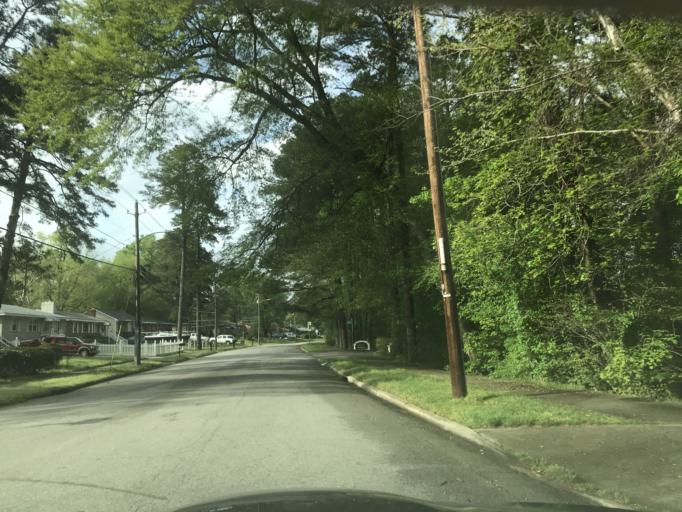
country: US
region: North Carolina
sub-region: Wake County
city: Raleigh
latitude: 35.7719
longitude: -78.6070
